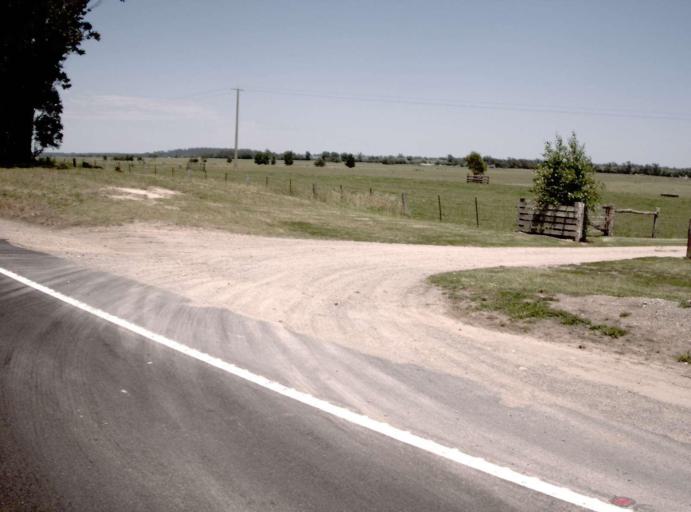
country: AU
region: Victoria
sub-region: East Gippsland
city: Lakes Entrance
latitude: -37.7028
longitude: 148.4870
